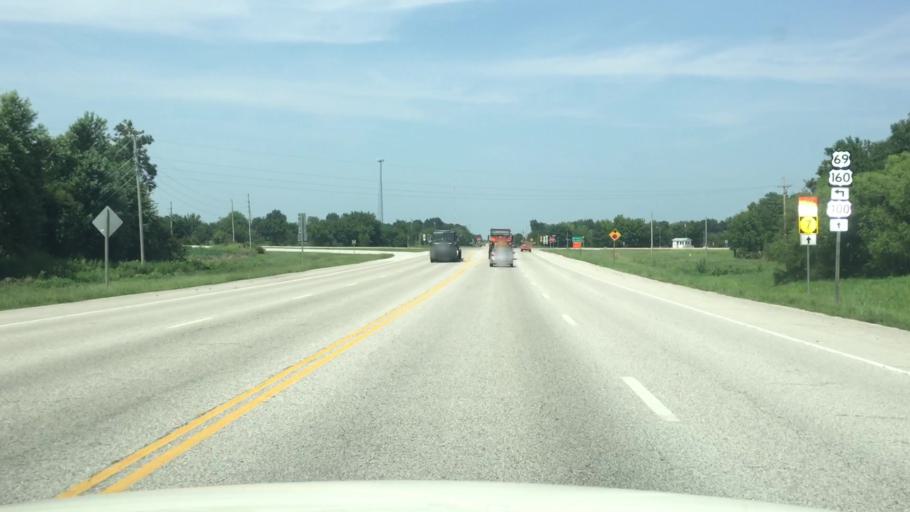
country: US
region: Kansas
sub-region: Cherokee County
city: Galena
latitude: 37.1756
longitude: -94.7044
